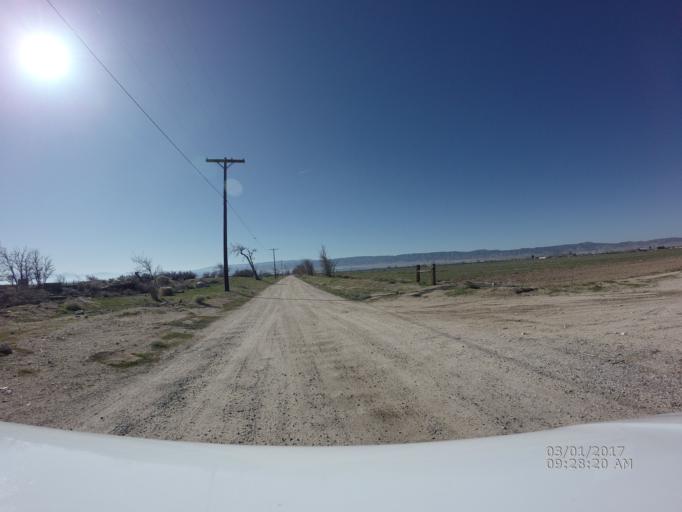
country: US
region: California
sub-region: Los Angeles County
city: Quartz Hill
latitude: 34.7258
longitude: -118.2723
